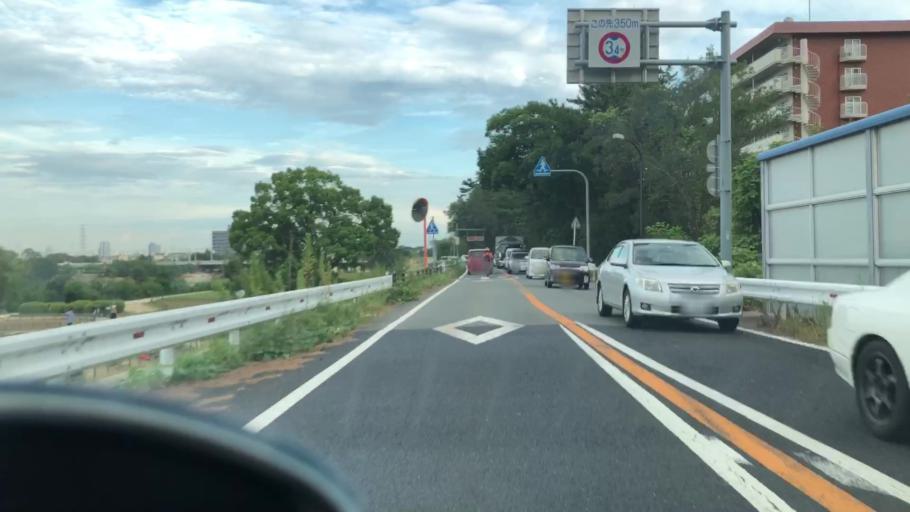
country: JP
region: Hyogo
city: Amagasaki
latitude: 34.7419
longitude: 135.3771
